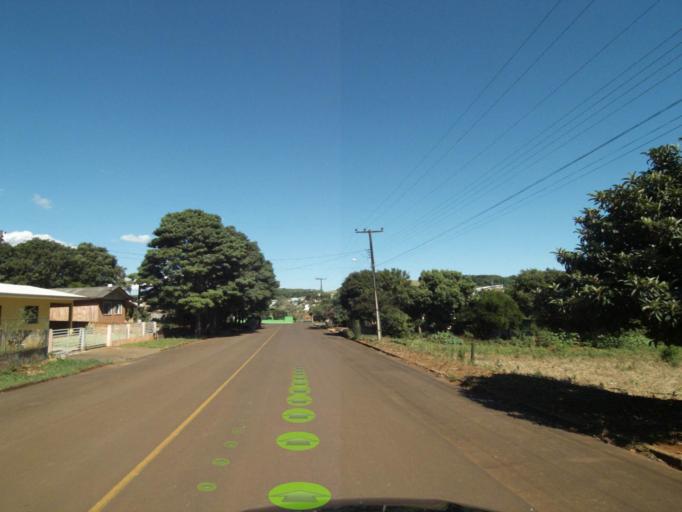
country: BR
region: Parana
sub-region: Coronel Vivida
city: Coronel Vivida
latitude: -26.1444
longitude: -52.3878
